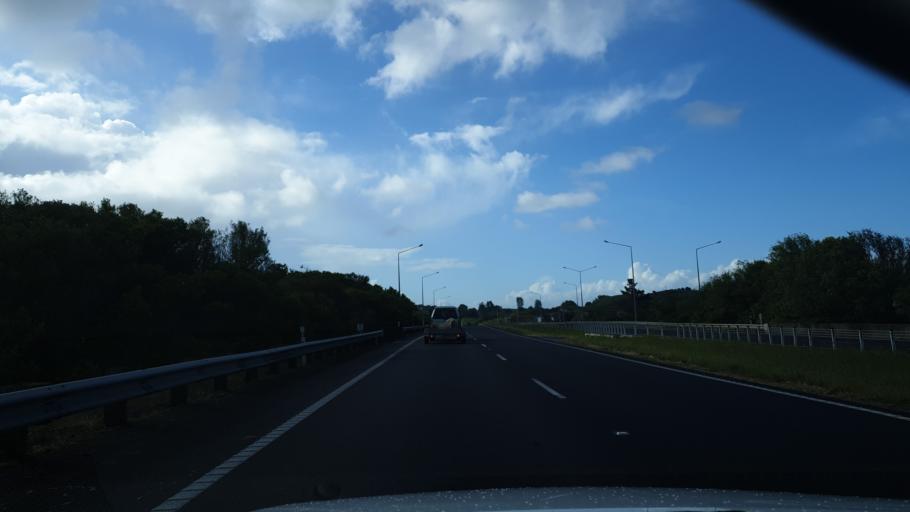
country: NZ
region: Auckland
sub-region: Auckland
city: Pukekohe East
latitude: -37.2478
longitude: 175.0277
